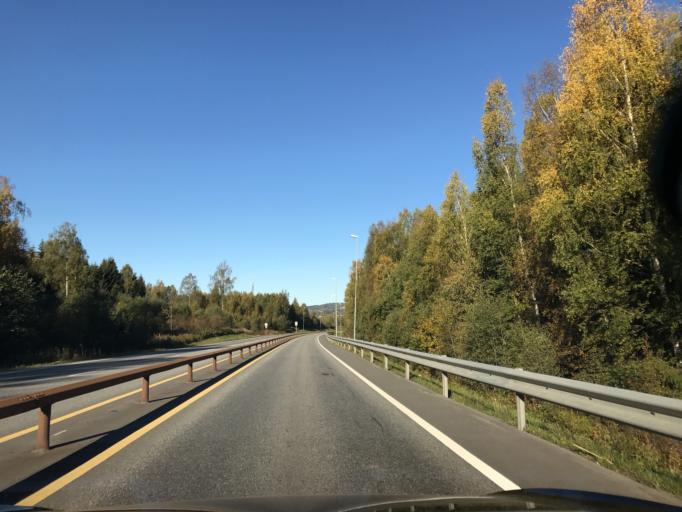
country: NO
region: Hedmark
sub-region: Hamar
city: Hamar
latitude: 60.7816
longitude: 11.1382
